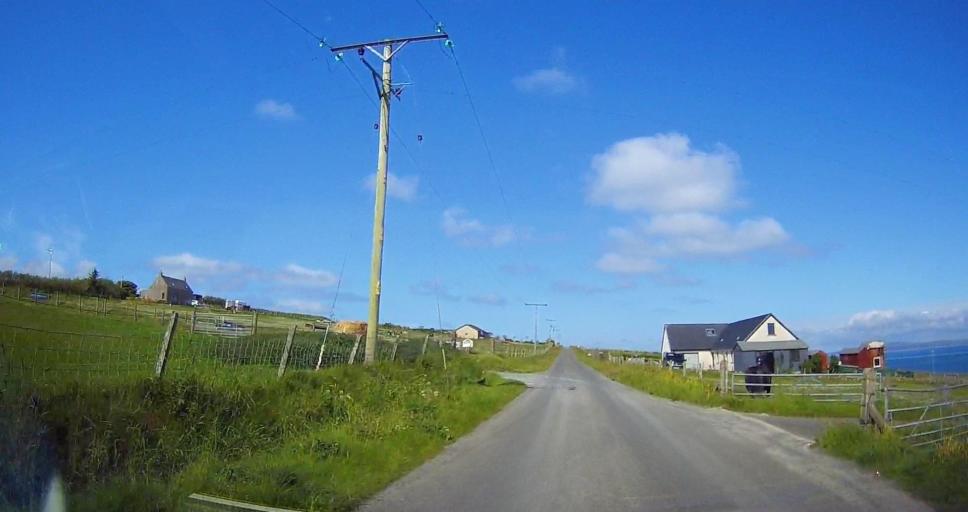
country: GB
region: Scotland
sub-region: Orkney Islands
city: Kirkwall
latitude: 58.8545
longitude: -2.9239
